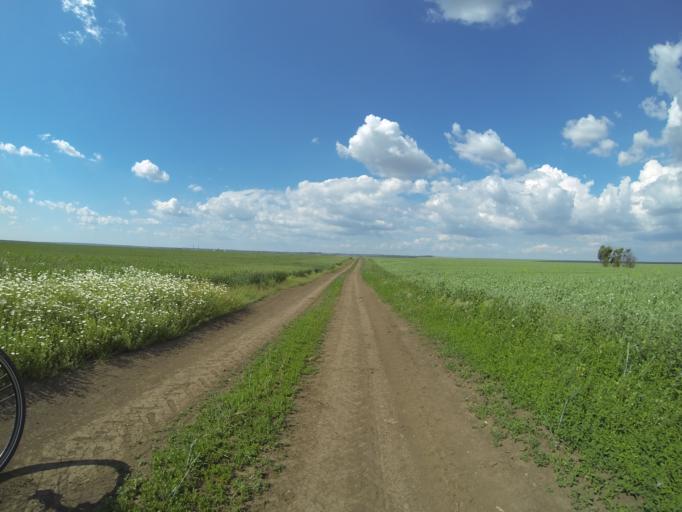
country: RO
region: Dolj
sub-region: Comuna Segarcea
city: Segarcea
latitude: 44.0528
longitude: 23.7445
